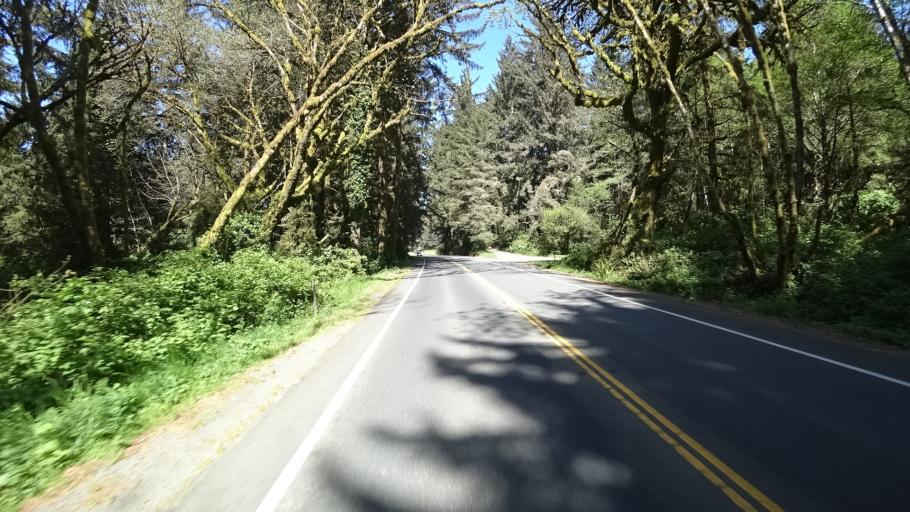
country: US
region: California
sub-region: Del Norte County
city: Bertsch-Oceanview
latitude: 41.5829
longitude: -124.0823
